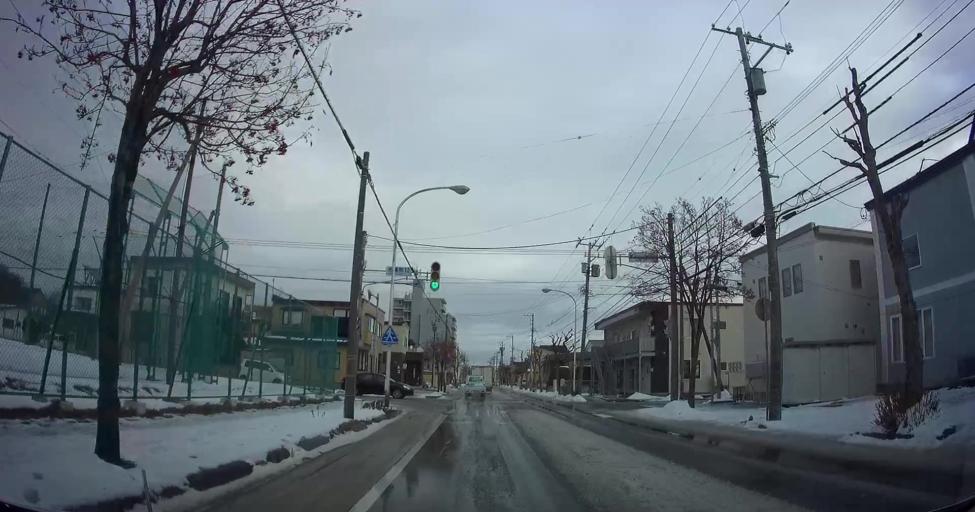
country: JP
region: Hokkaido
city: Hakodate
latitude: 41.7784
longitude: 140.7520
